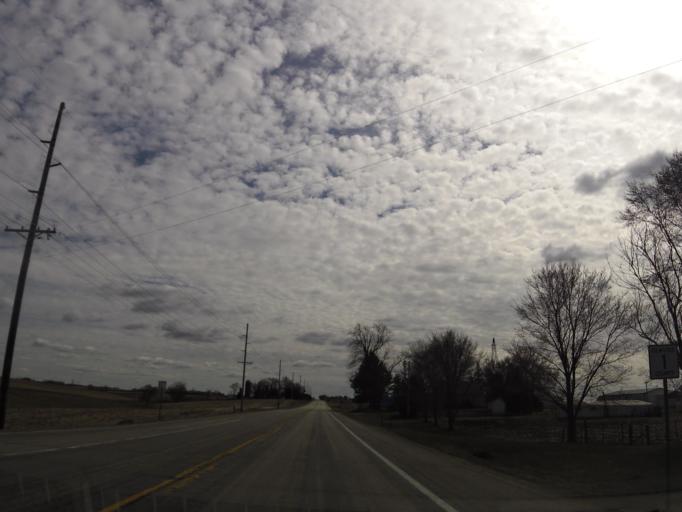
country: US
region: Minnesota
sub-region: Olmsted County
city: Rochester
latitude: 43.9417
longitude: -92.4087
